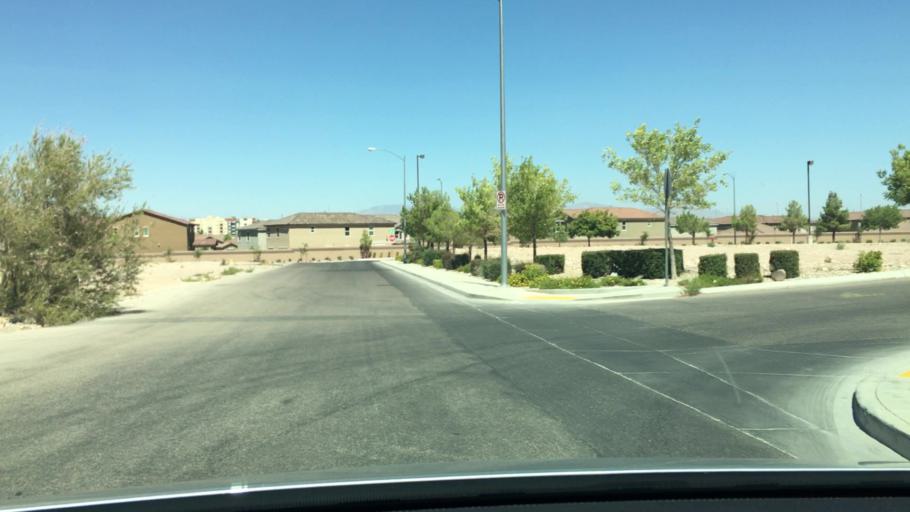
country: US
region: Nevada
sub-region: Clark County
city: Summerlin South
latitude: 36.0748
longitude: -115.2931
